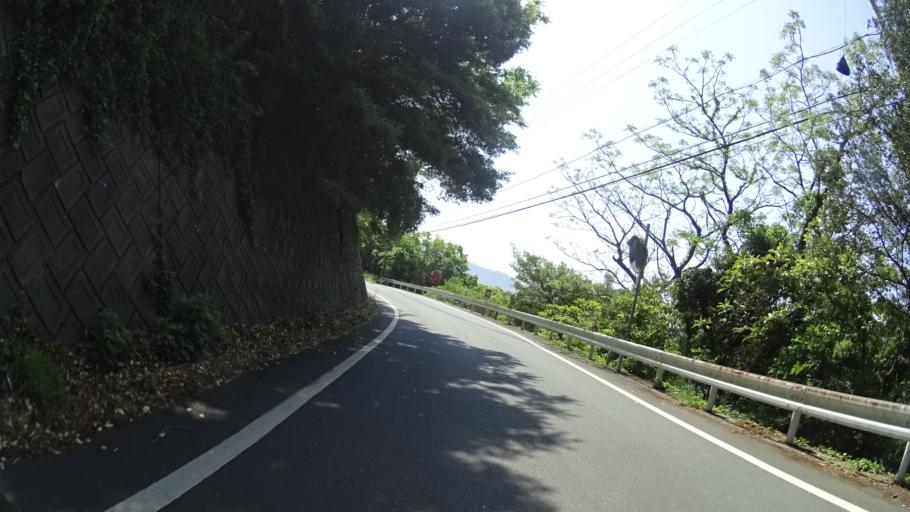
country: JP
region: Ehime
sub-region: Nishiuwa-gun
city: Ikata-cho
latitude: 33.3892
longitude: 132.0953
